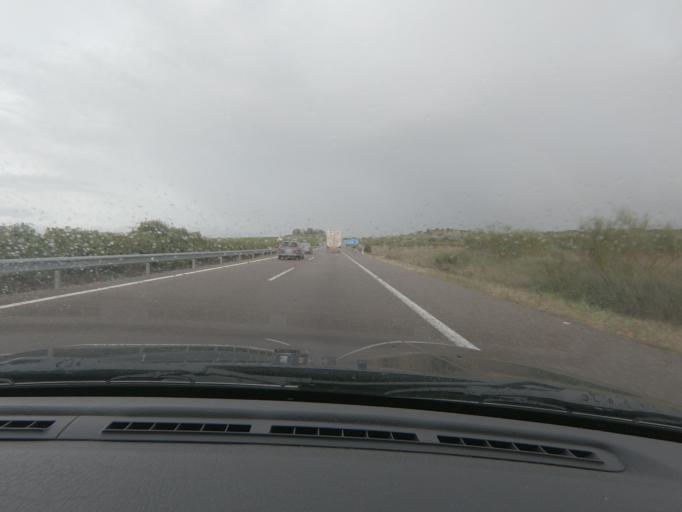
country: ES
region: Extremadura
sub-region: Provincia de Badajoz
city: Talavera La Real
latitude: 38.8681
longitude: -6.8330
